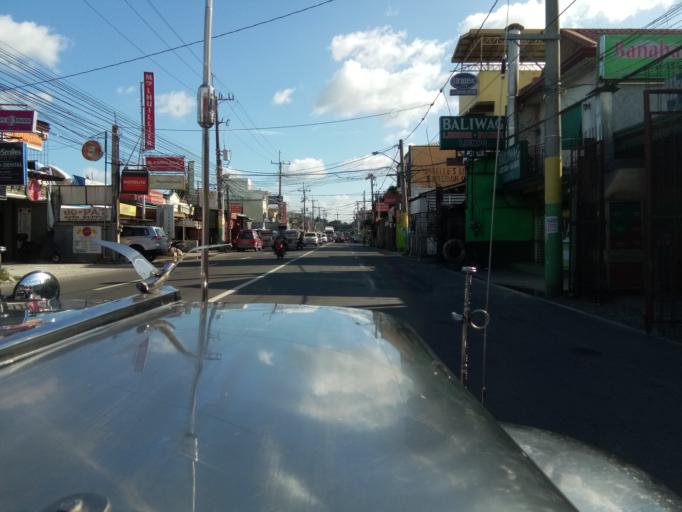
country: PH
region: Calabarzon
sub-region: Province of Cavite
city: Dasmarinas
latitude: 14.3476
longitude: 120.9813
